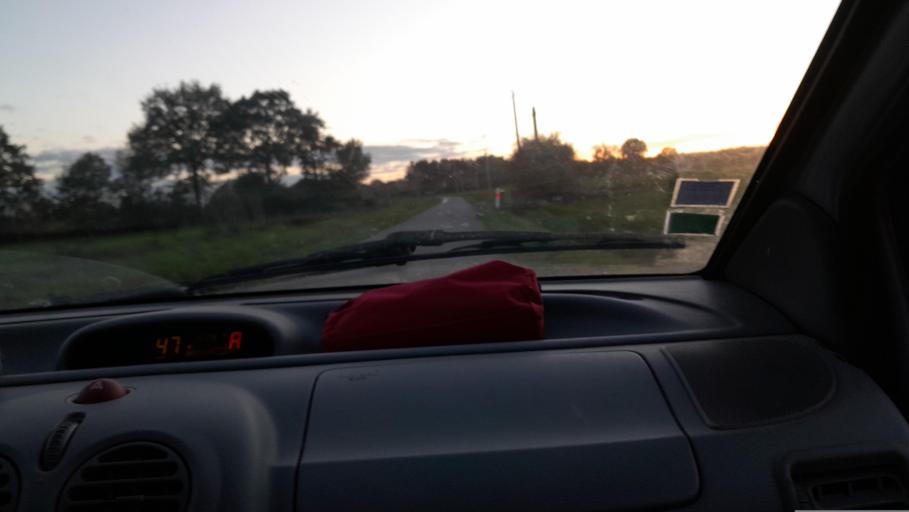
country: FR
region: Brittany
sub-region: Departement d'Ille-et-Vilaine
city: Rannee
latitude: 47.8817
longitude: -1.1802
